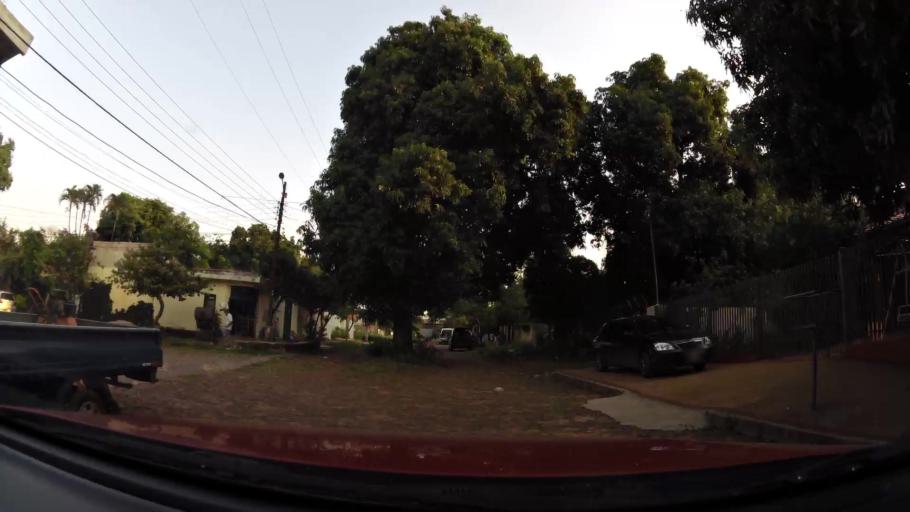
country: PY
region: Central
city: Lambare
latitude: -25.3514
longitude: -57.6026
